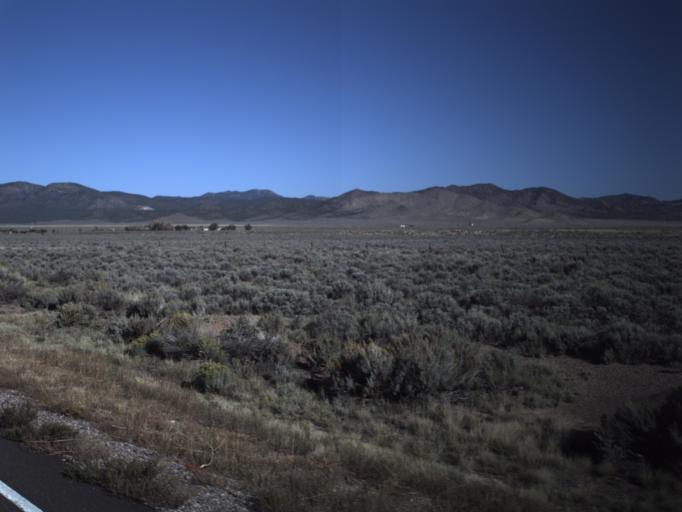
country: US
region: Utah
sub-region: Washington County
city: Enterprise
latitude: 37.7892
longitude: -113.8838
